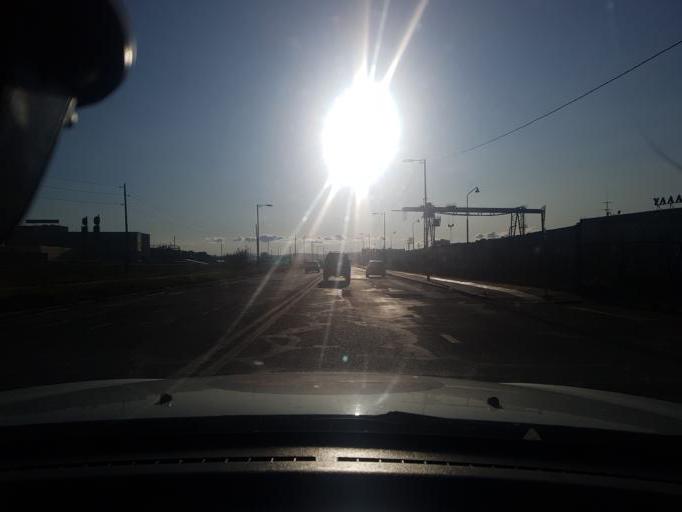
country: MN
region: Ulaanbaatar
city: Ulaanbaatar
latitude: 47.9098
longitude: 106.7949
